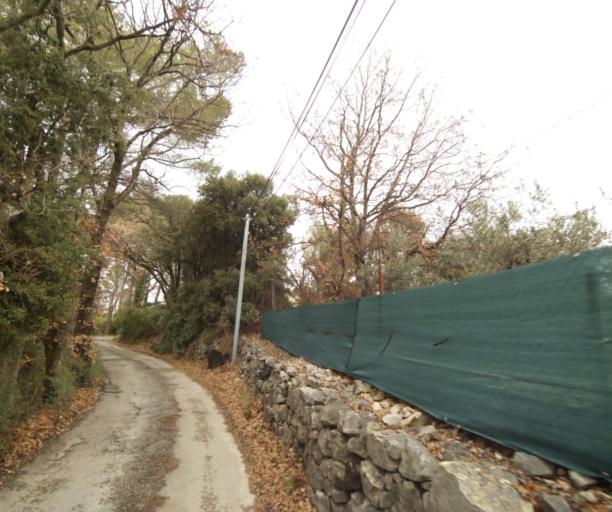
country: FR
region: Provence-Alpes-Cote d'Azur
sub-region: Departement du Var
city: Trans-en-Provence
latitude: 43.5085
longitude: 6.4909
